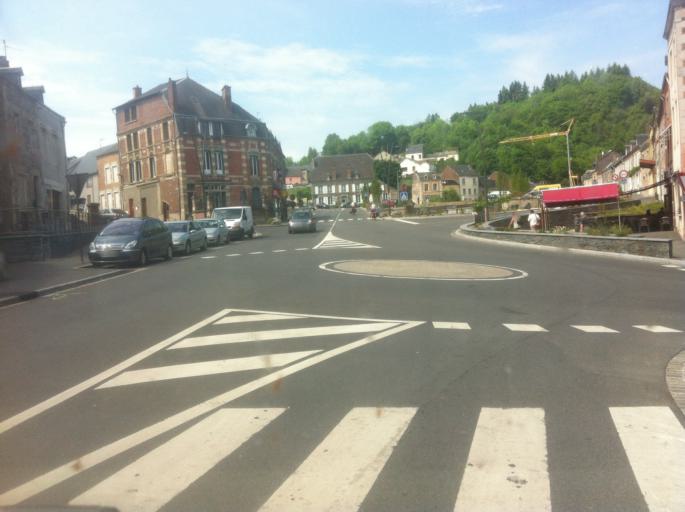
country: FR
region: Champagne-Ardenne
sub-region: Departement des Ardennes
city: Fumay
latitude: 49.9925
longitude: 4.7040
